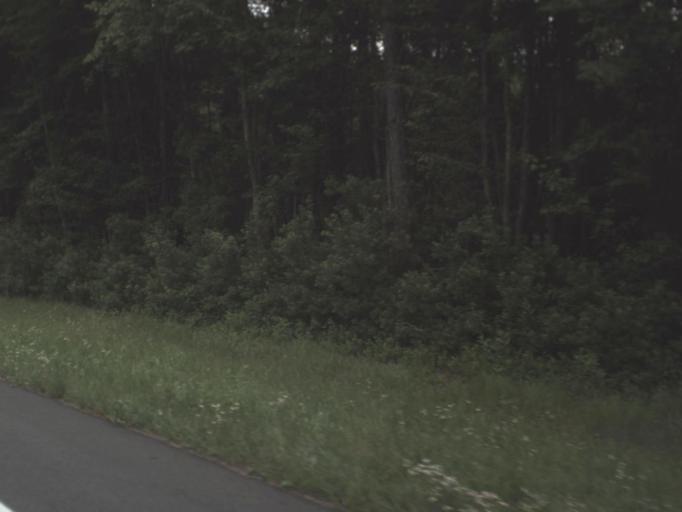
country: US
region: Florida
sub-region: Hamilton County
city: Jasper
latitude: 30.5604
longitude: -82.6806
